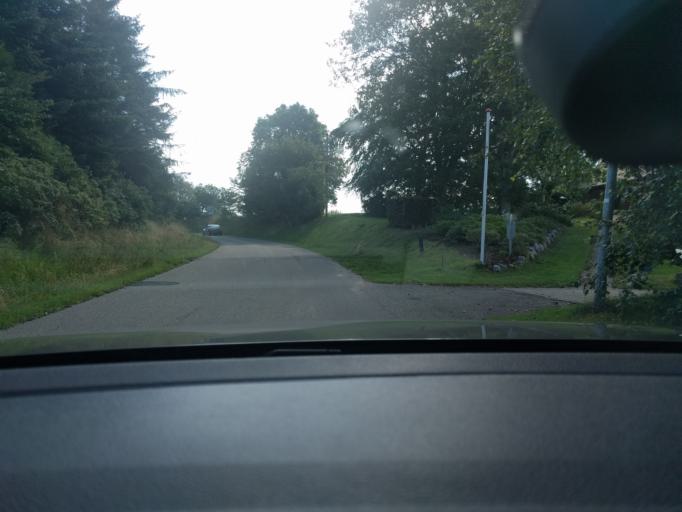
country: DK
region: Central Jutland
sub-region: Viborg Kommune
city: Viborg
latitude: 56.5293
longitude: 9.3235
